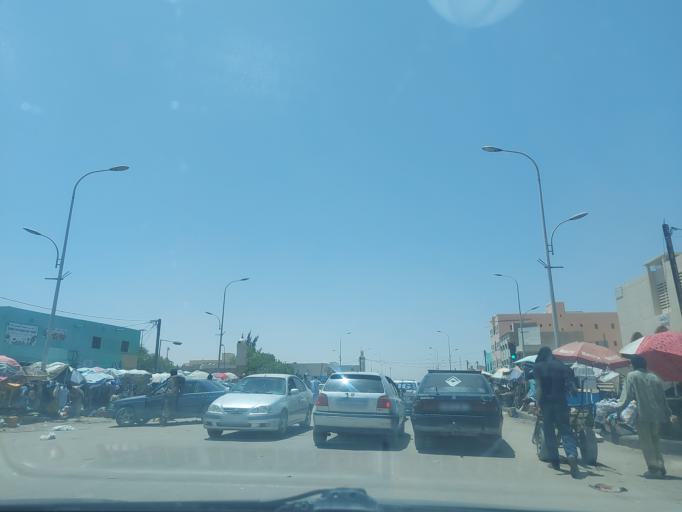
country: MR
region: Nouakchott
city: Nouakchott
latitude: 18.0826
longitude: -15.9813
